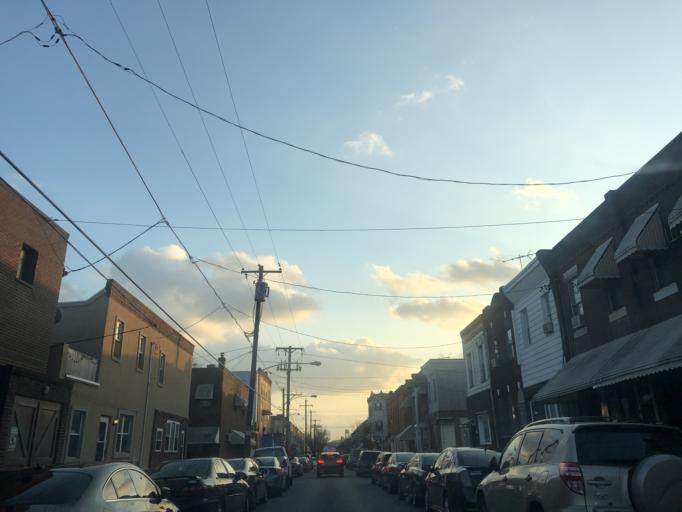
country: US
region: Pennsylvania
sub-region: Philadelphia County
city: Philadelphia
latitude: 39.9218
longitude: -75.1632
